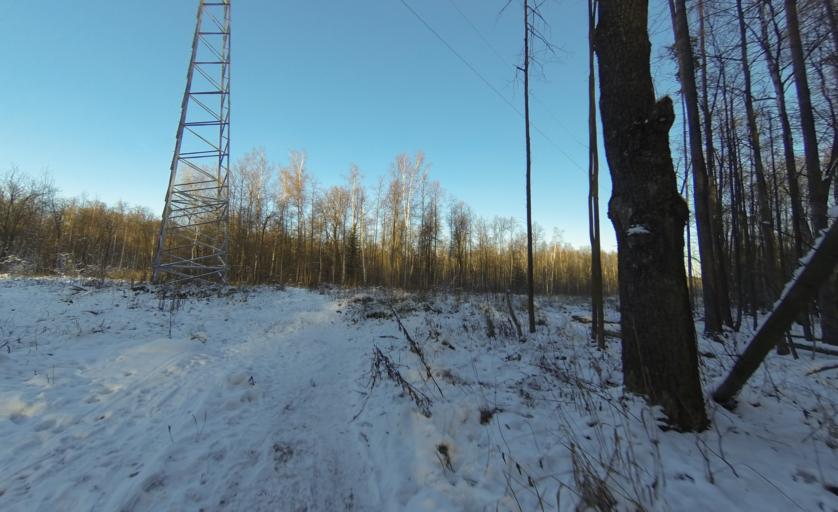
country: RU
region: Moscow
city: Babushkin
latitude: 55.8457
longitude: 37.7623
